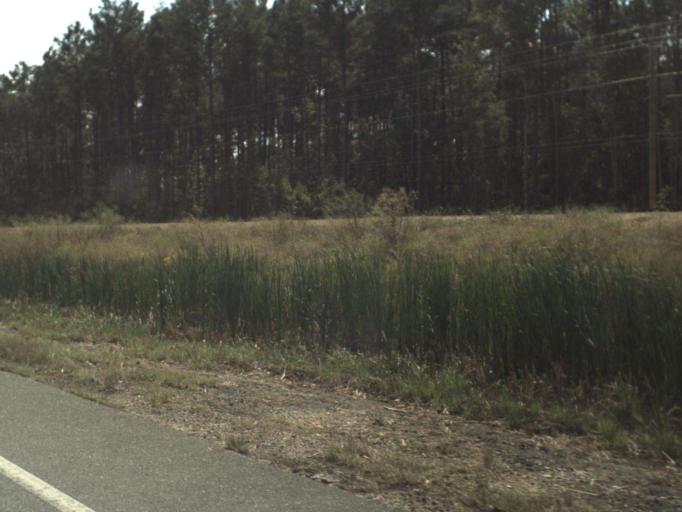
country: US
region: Florida
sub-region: Holmes County
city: Bonifay
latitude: 30.6544
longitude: -85.6990
